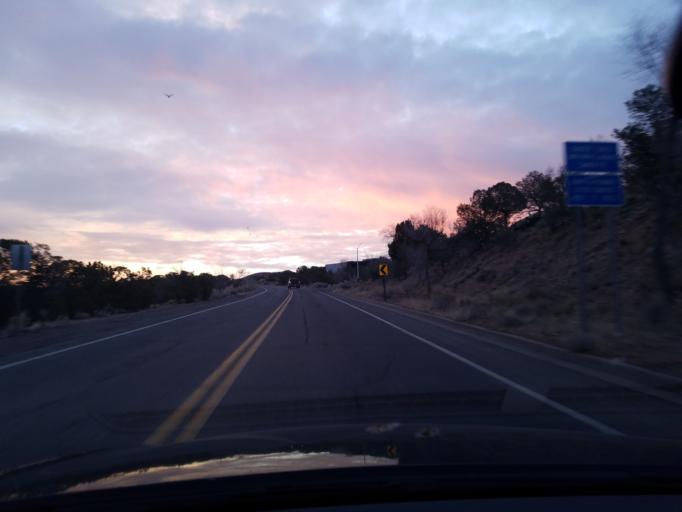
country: US
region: New Mexico
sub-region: Santa Fe County
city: Santa Fe
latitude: 35.6920
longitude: -105.9309
